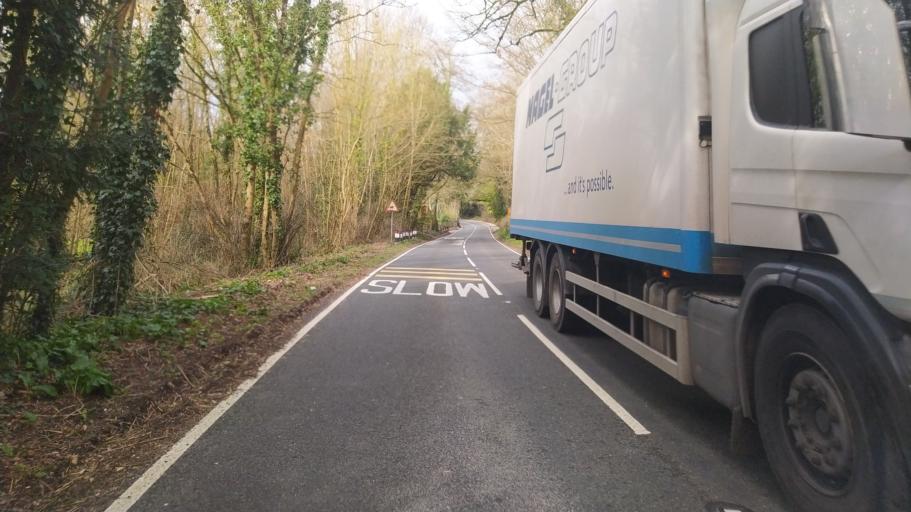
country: GB
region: England
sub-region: Dorset
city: Dorchester
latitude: 50.7506
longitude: -2.5177
